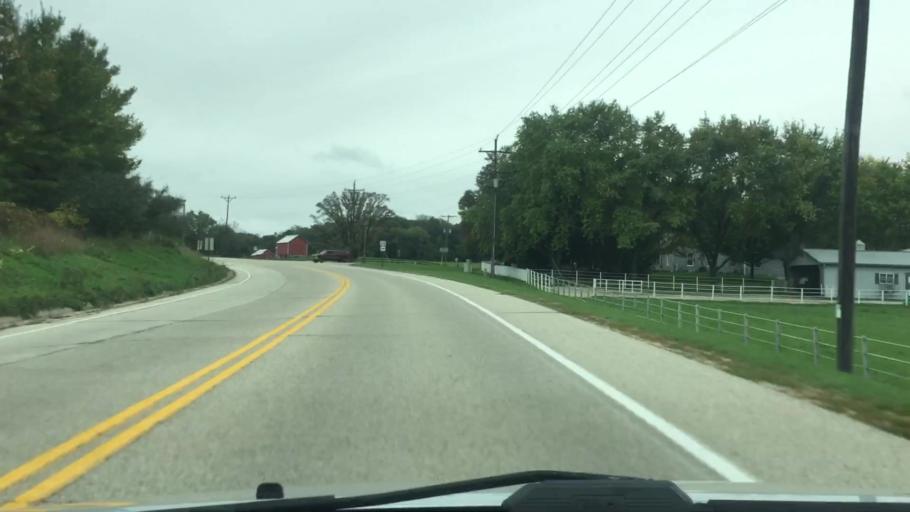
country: US
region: Wisconsin
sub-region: Waukesha County
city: Eagle
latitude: 42.8566
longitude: -88.5069
